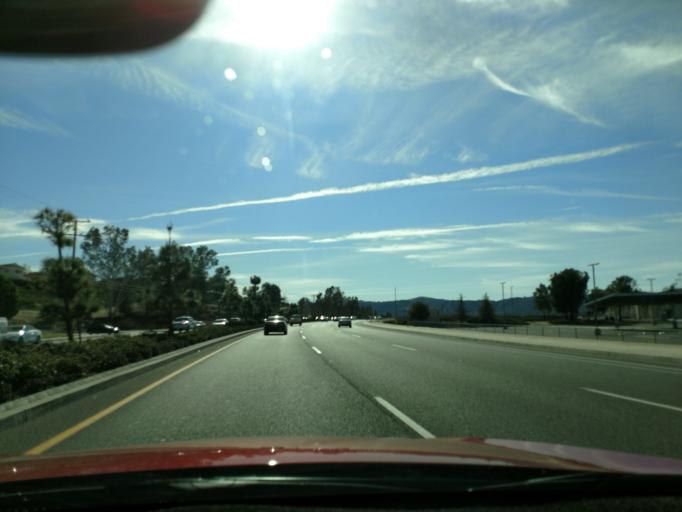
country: US
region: California
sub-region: Riverside County
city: Murrieta Hot Springs
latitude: 33.5379
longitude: -117.1451
